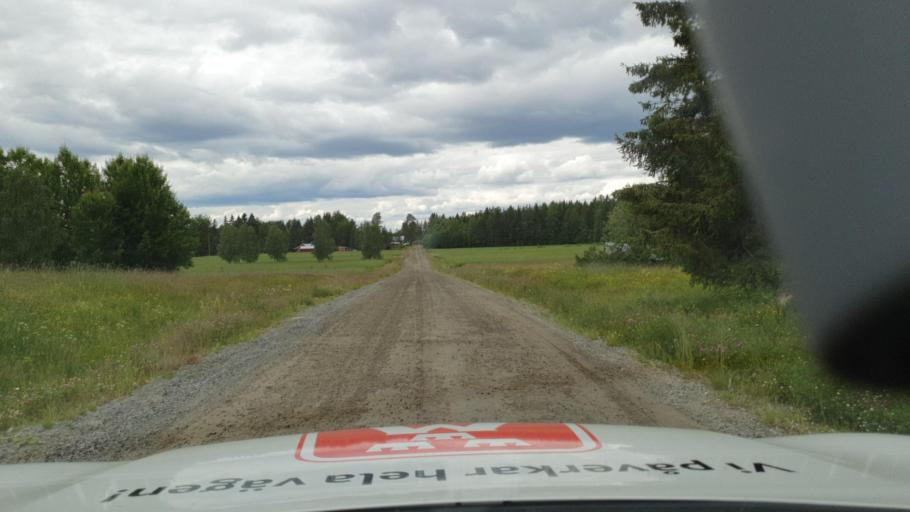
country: SE
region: Vaesterbotten
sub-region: Bjurholms Kommun
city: Bjurholm
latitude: 63.7935
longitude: 19.0961
